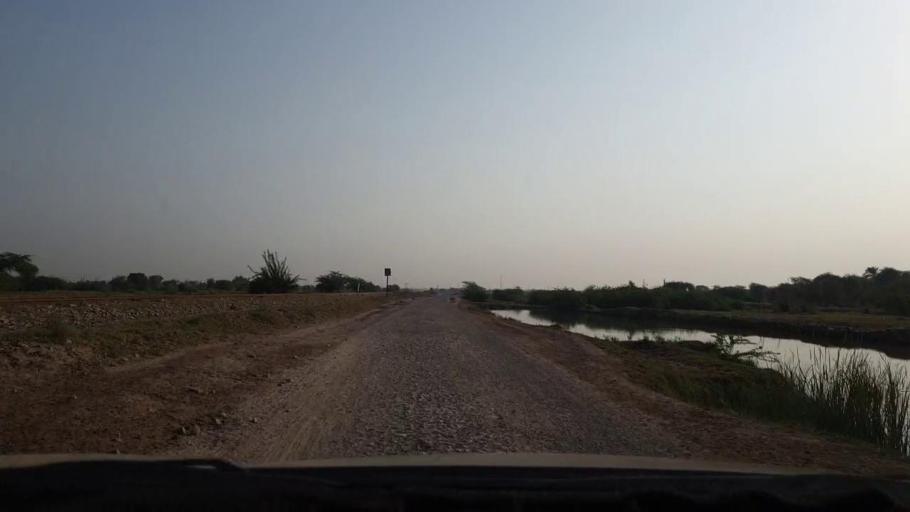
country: PK
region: Sindh
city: Larkana
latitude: 27.5210
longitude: 68.1917
